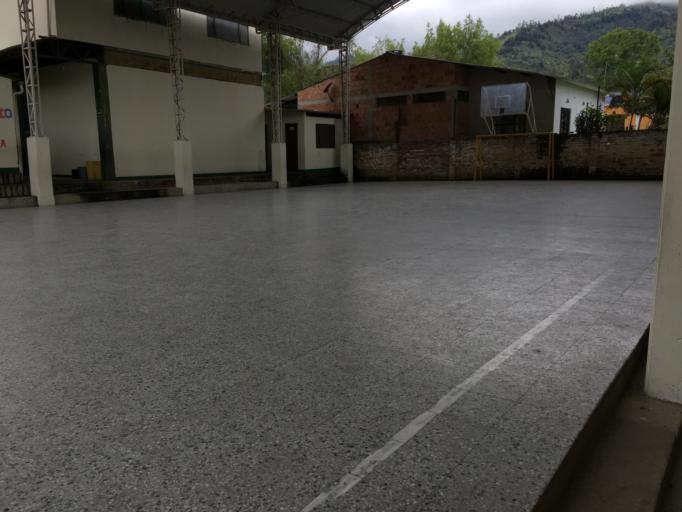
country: CO
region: Cundinamarca
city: Tenza
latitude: 5.0958
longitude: -73.4434
